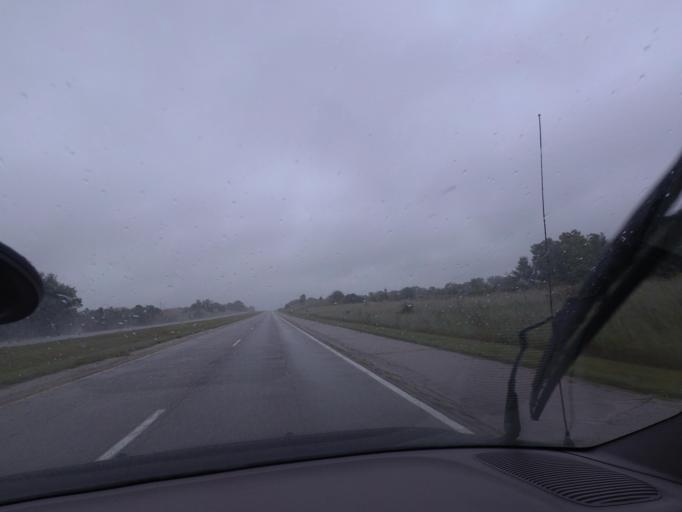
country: US
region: Illinois
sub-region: Pike County
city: Pittsfield
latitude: 39.6886
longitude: -90.9065
